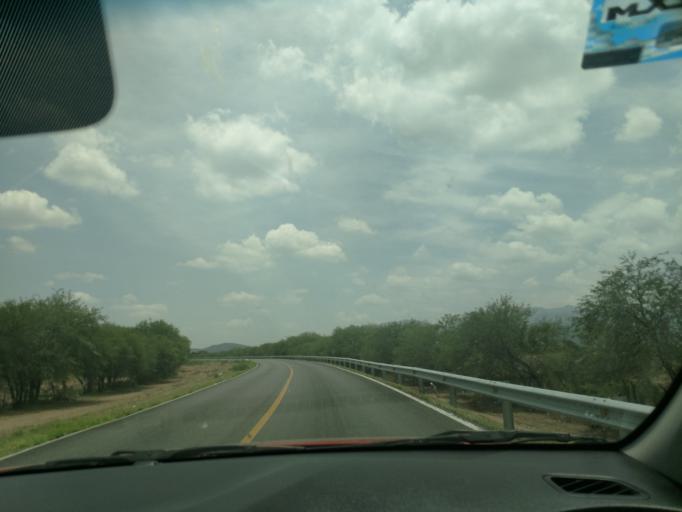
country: MX
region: San Luis Potosi
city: Zaragoza
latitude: 22.0192
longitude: -100.4000
